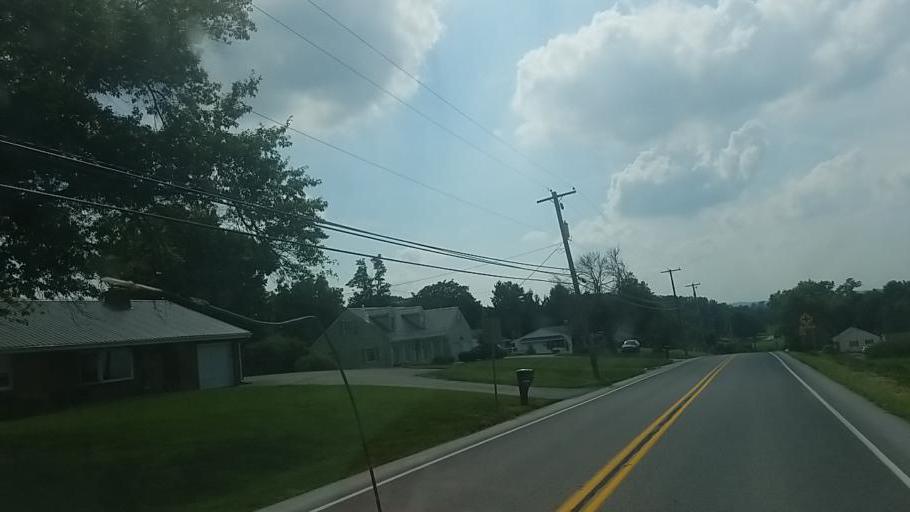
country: US
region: Pennsylvania
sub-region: Lancaster County
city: Strasburg
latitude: 39.9708
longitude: -76.1444
